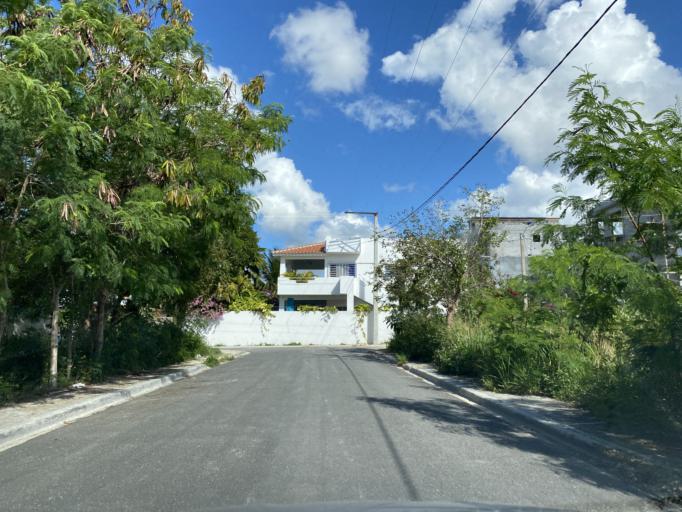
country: DO
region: La Romana
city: La Romana
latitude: 18.3691
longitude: -68.8358
